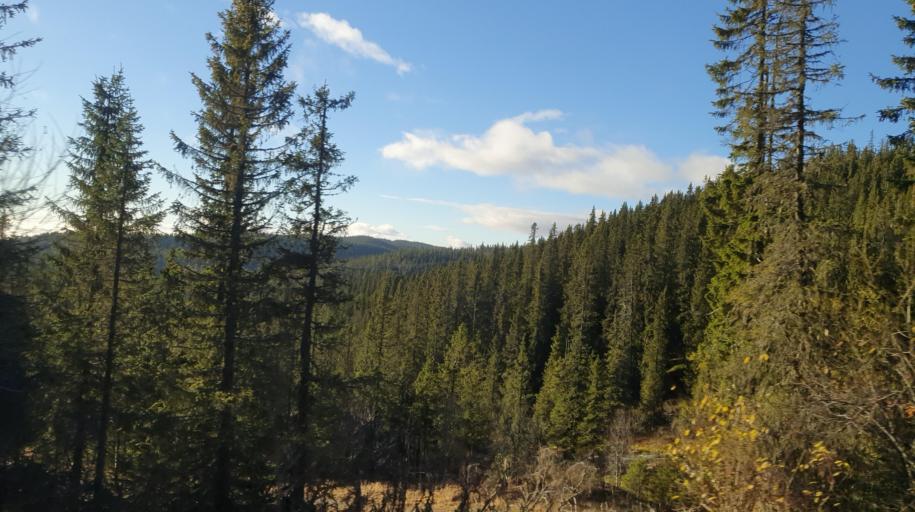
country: NO
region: Buskerud
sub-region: Krodsherad
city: Noresund
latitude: 60.2229
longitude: 9.5314
